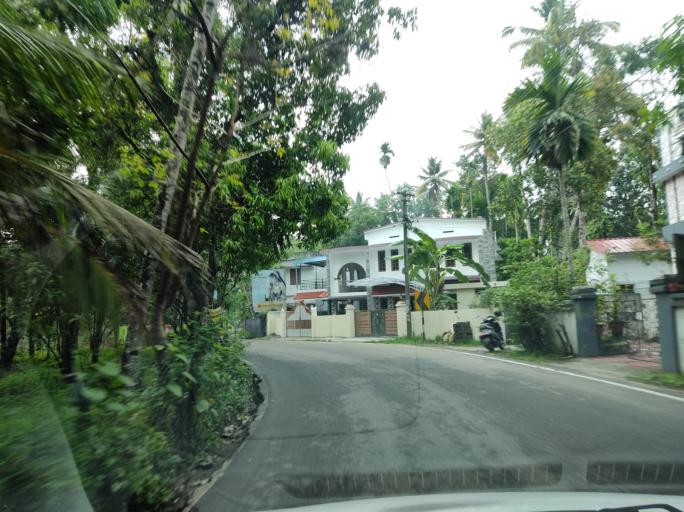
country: IN
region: Kerala
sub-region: Alappuzha
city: Kayankulam
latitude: 9.1949
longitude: 76.4669
